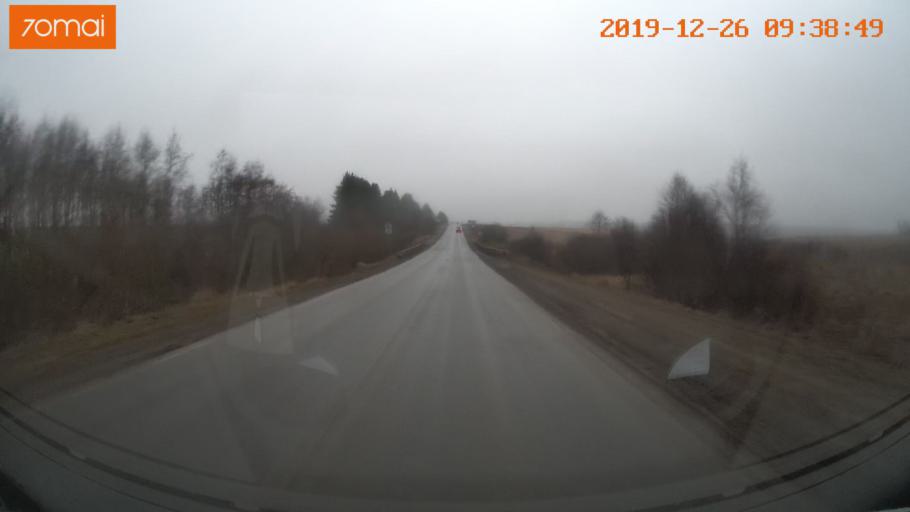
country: RU
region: Vologda
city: Vologda
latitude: 59.1482
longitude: 40.0356
